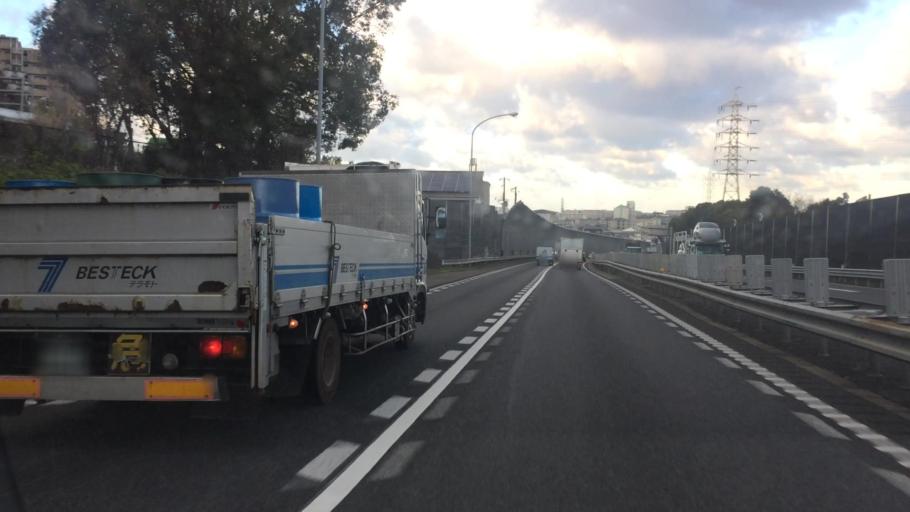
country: JP
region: Hyogo
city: Akashi
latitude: 34.6486
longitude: 135.0500
